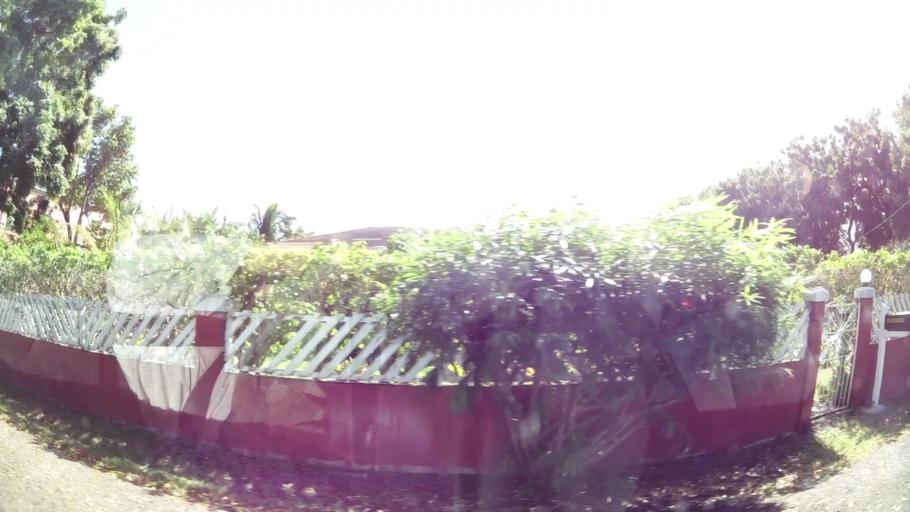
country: AG
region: Saint George
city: Piggotts
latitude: 17.1674
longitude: -61.8081
